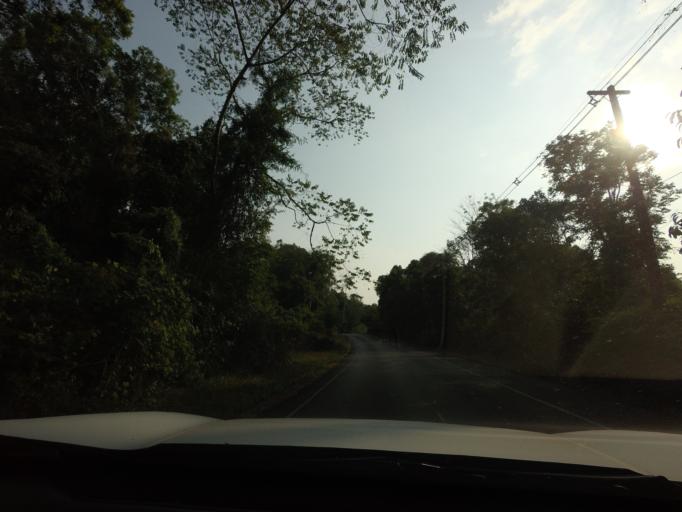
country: TH
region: Nakhon Nayok
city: Nakhon Nayok
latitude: 14.4147
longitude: 101.3784
